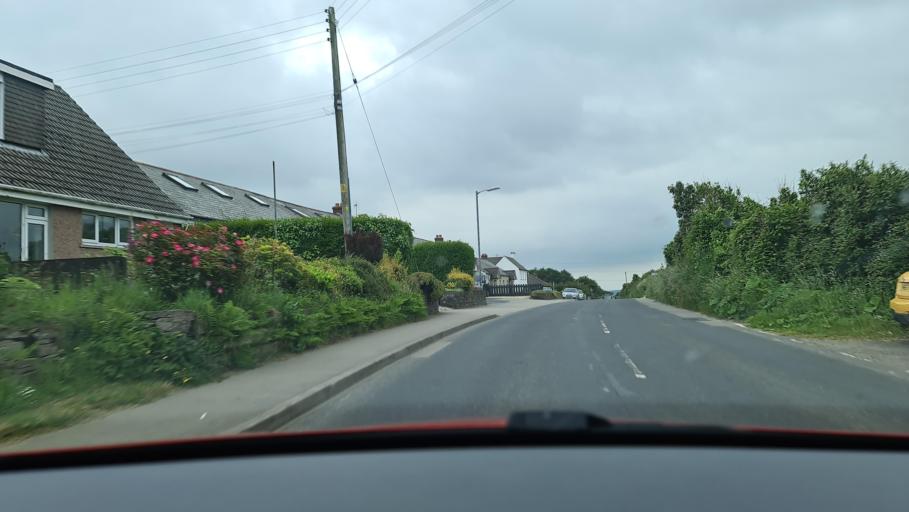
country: GB
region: England
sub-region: Cornwall
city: Camelford
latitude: 50.6173
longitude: -4.6860
